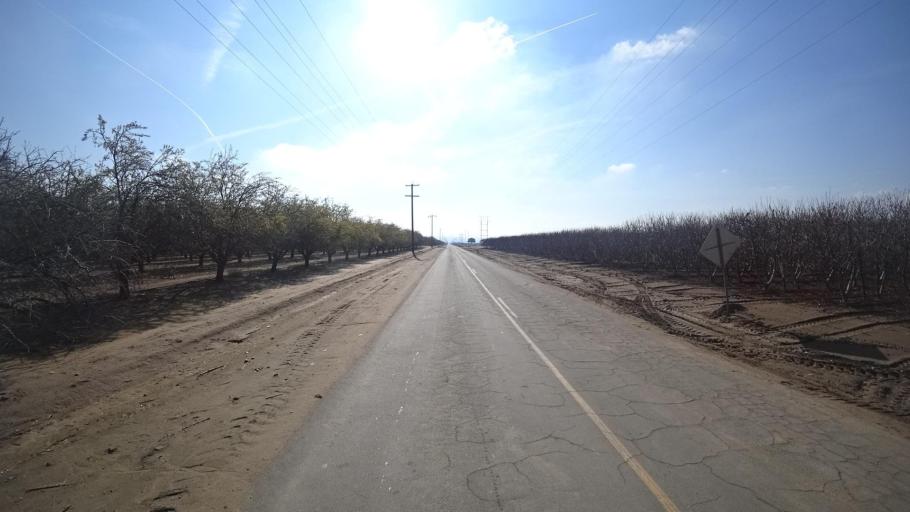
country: US
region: California
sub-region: Kern County
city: Arvin
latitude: 35.2381
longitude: -118.8067
